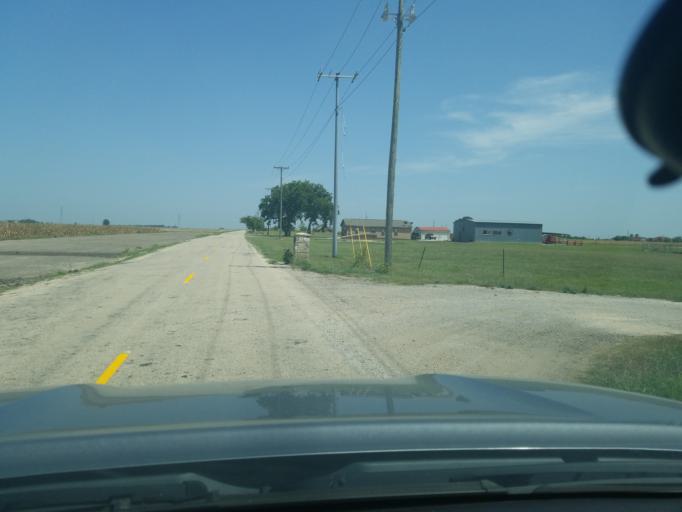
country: US
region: Texas
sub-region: Guadalupe County
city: Lake Dunlap
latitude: 29.6820
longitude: -98.0300
